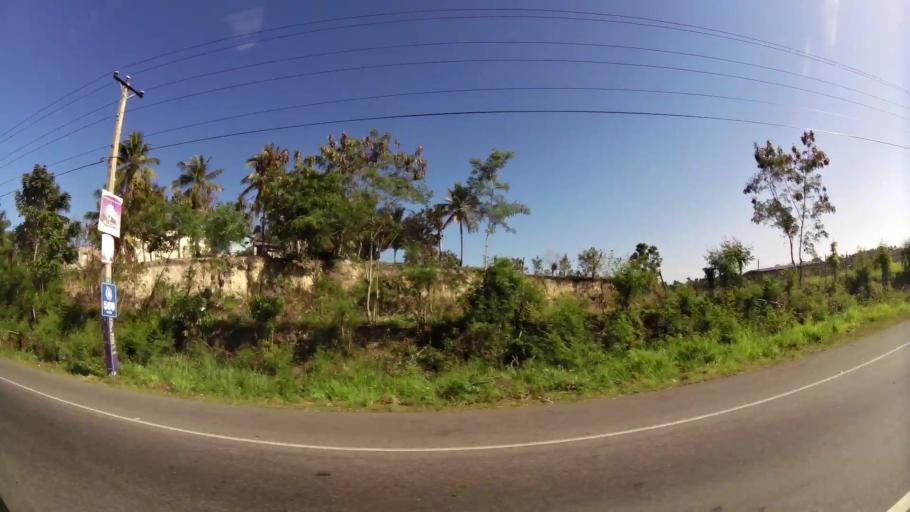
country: DO
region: San Cristobal
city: San Cristobal
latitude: 18.4341
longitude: -70.0775
